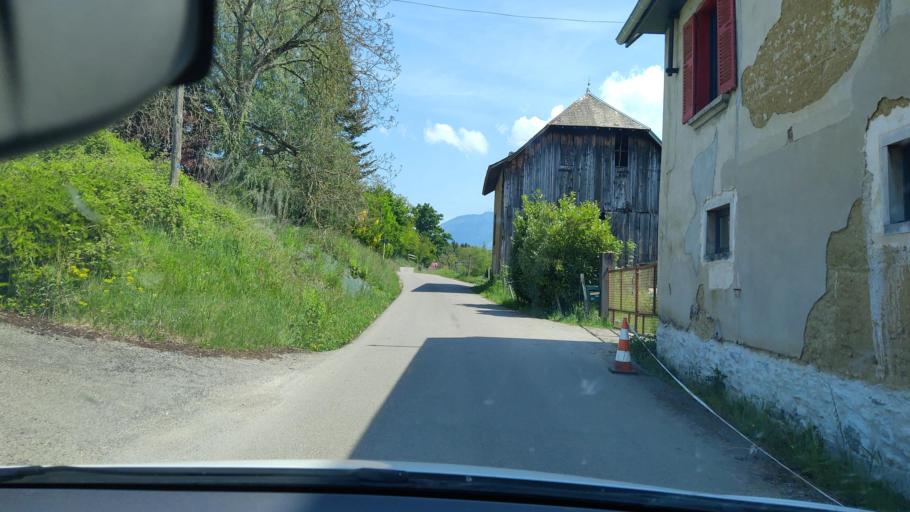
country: FR
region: Rhone-Alpes
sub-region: Departement de la Savoie
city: Domessin
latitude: 45.5296
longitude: 5.7025
